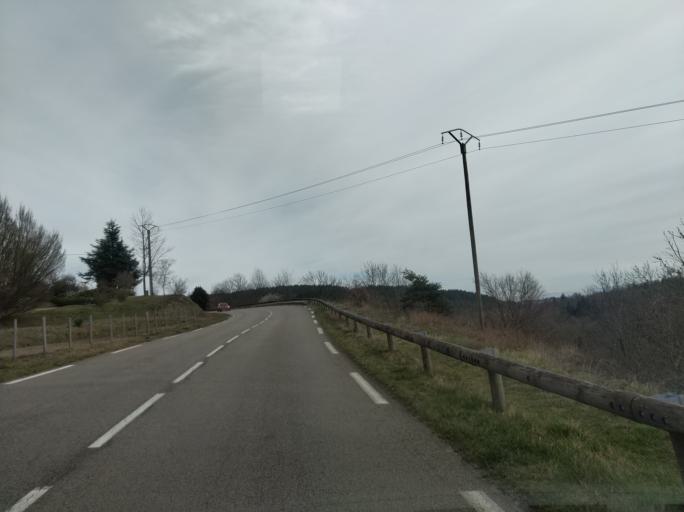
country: FR
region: Rhone-Alpes
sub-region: Departement de l'Ardeche
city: Satillieu
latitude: 45.1612
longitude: 4.6341
